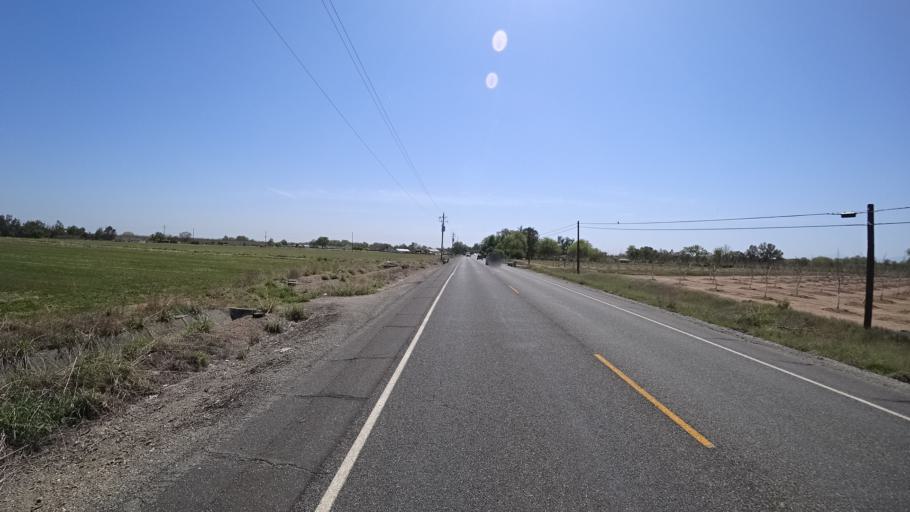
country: US
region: California
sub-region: Glenn County
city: Orland
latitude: 39.7721
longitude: -122.1968
